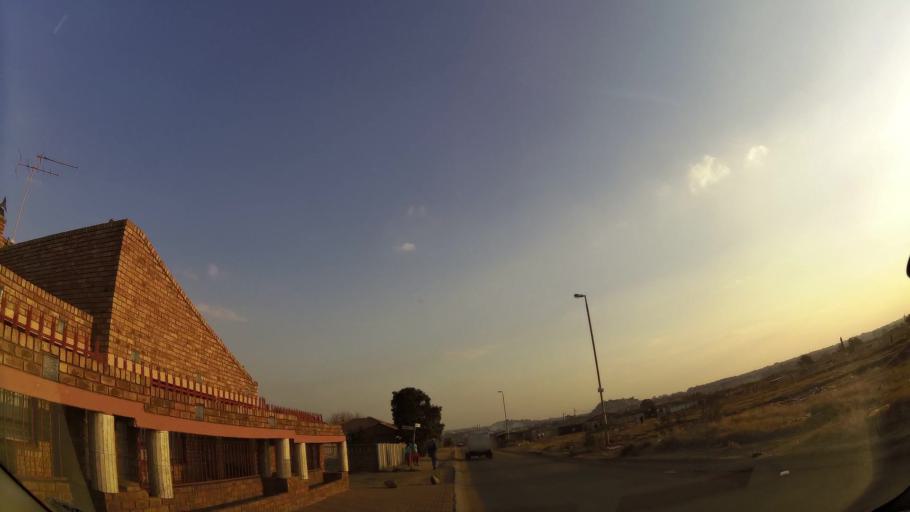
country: ZA
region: Gauteng
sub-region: Ekurhuleni Metropolitan Municipality
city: Benoni
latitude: -26.1601
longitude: 28.3763
